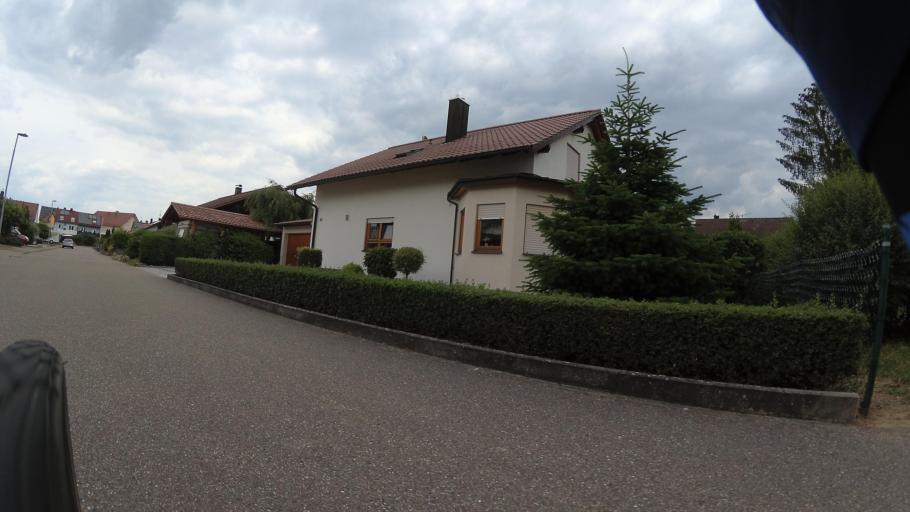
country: DE
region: Baden-Wuerttemberg
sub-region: Regierungsbezirk Stuttgart
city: Oedheim
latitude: 49.2688
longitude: 9.2263
